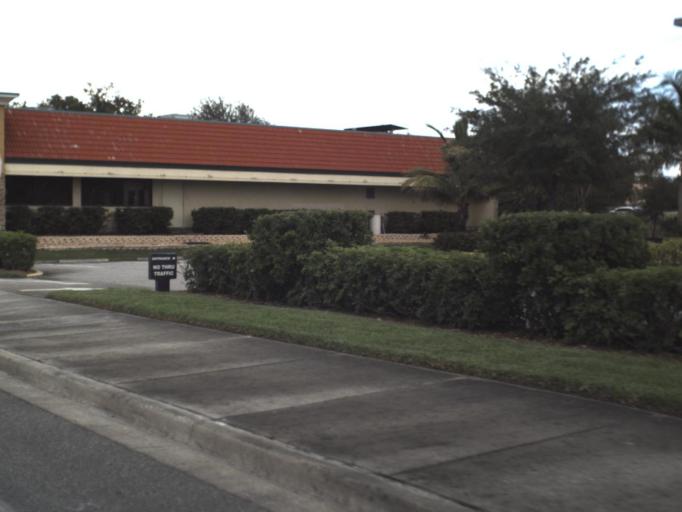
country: US
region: Florida
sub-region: Sarasota County
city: Venice Gardens
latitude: 27.0794
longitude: -82.4247
